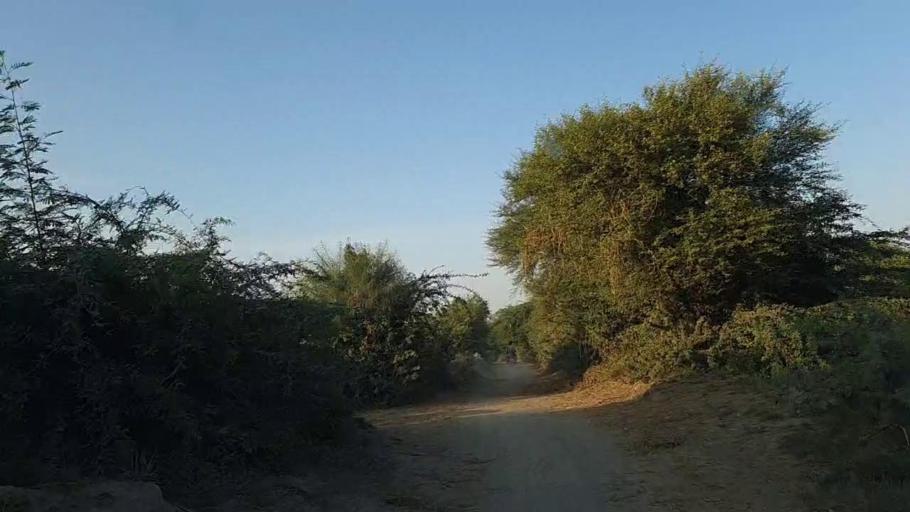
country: PK
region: Sindh
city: Mirpur Batoro
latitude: 24.7148
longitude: 68.2147
